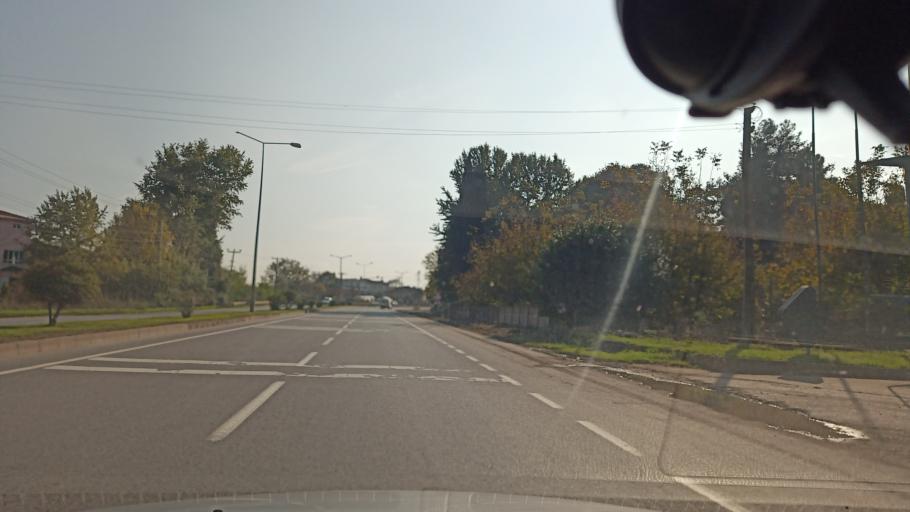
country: TR
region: Sakarya
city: Adapazari
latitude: 40.8135
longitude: 30.4038
